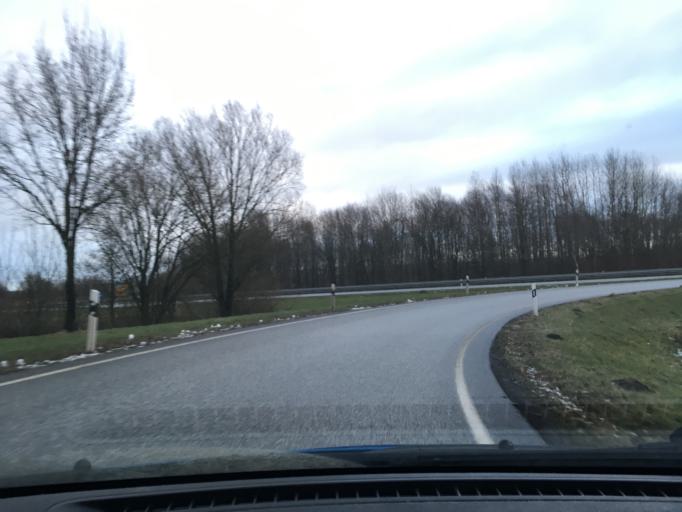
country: DE
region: Schleswig-Holstein
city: Ottenbuttel
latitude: 53.9586
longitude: 9.4895
